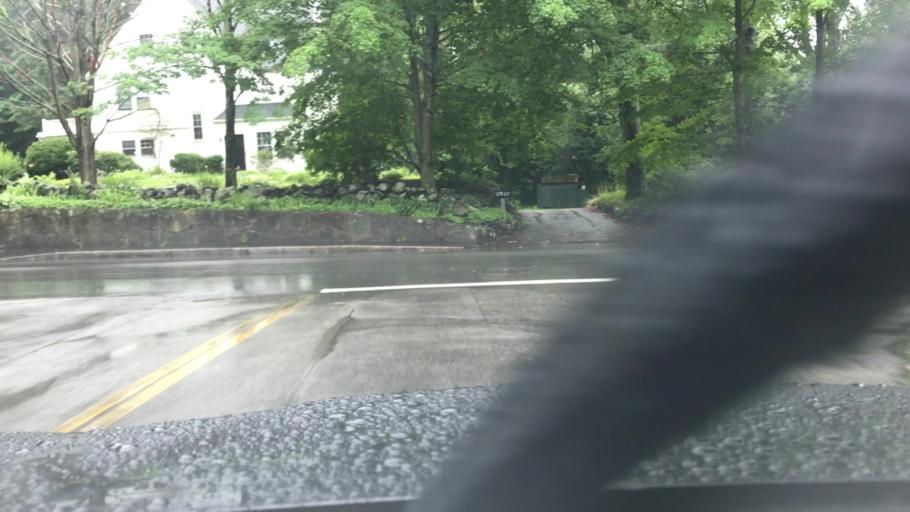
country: US
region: New Hampshire
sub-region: Strafford County
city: Durham
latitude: 43.1307
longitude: -70.9321
